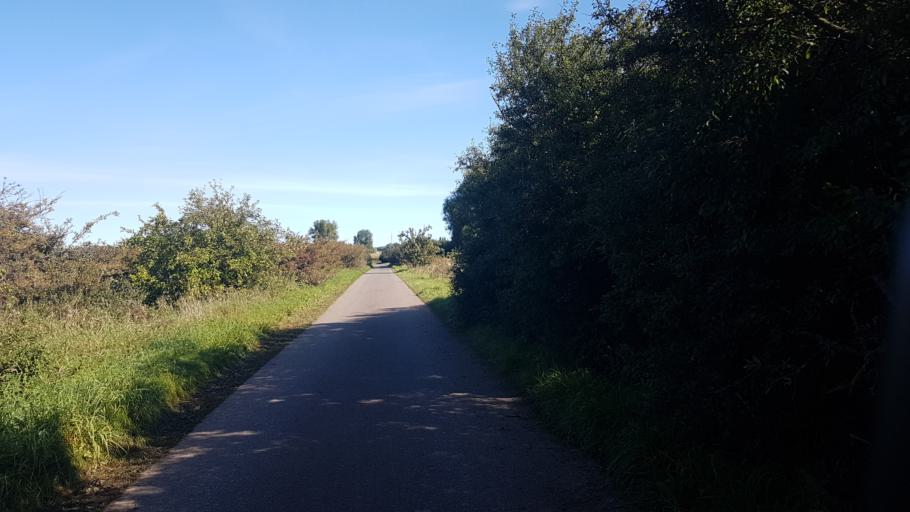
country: DE
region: Mecklenburg-Vorpommern
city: Sagard
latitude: 54.5121
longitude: 13.5285
